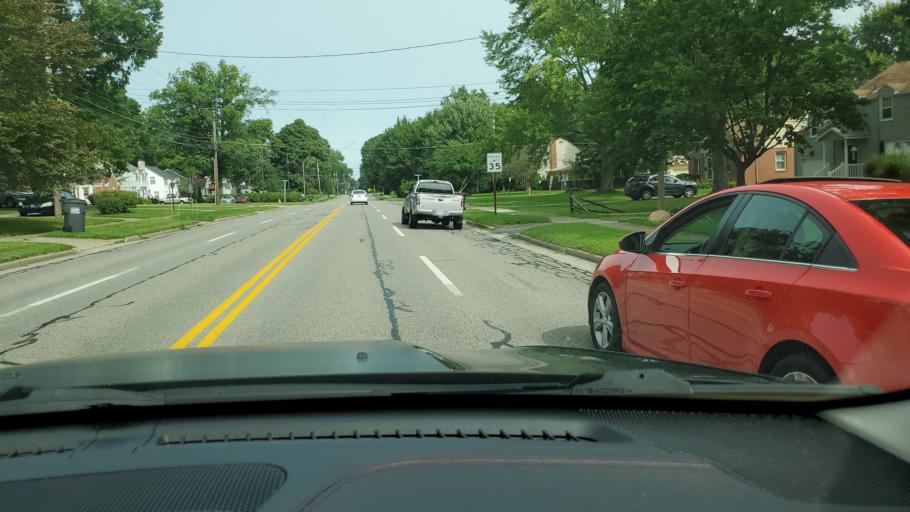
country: US
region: Ohio
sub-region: Mahoning County
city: Boardman
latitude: 41.0299
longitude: -80.6723
